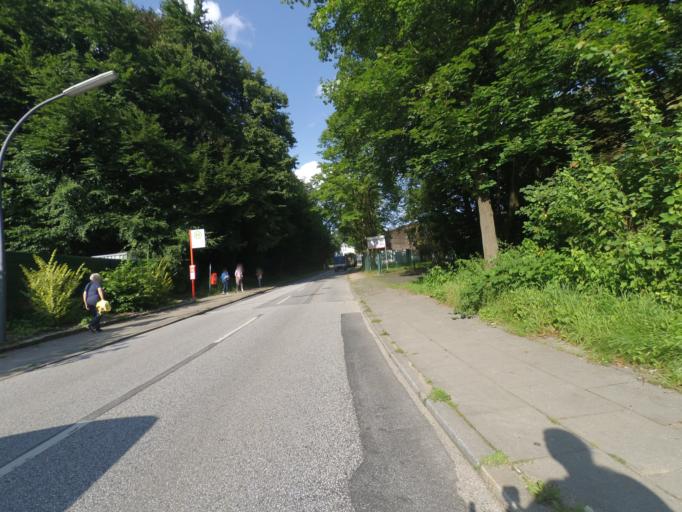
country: DE
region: Schleswig-Holstein
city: Oststeinbek
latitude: 53.5304
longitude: 10.1294
